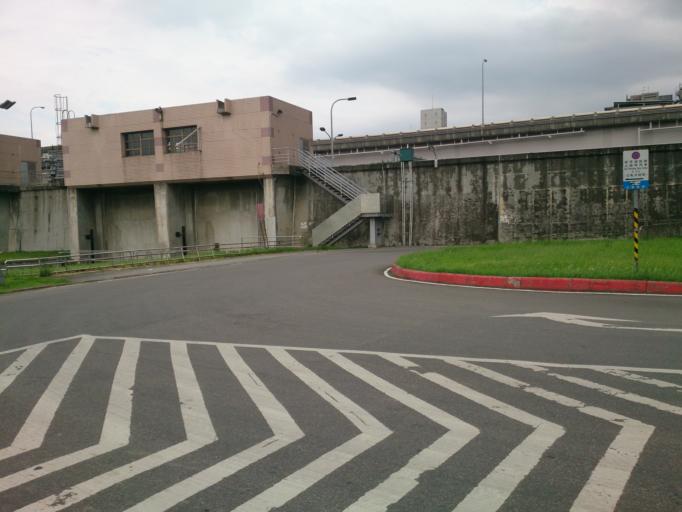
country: TW
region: Taipei
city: Taipei
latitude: 25.0602
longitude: 121.5725
